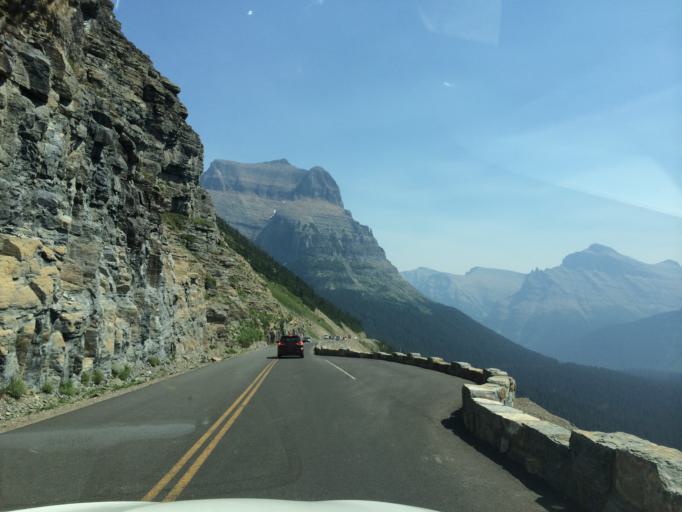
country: US
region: Montana
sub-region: Flathead County
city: Columbia Falls
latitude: 48.6969
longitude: -113.6920
